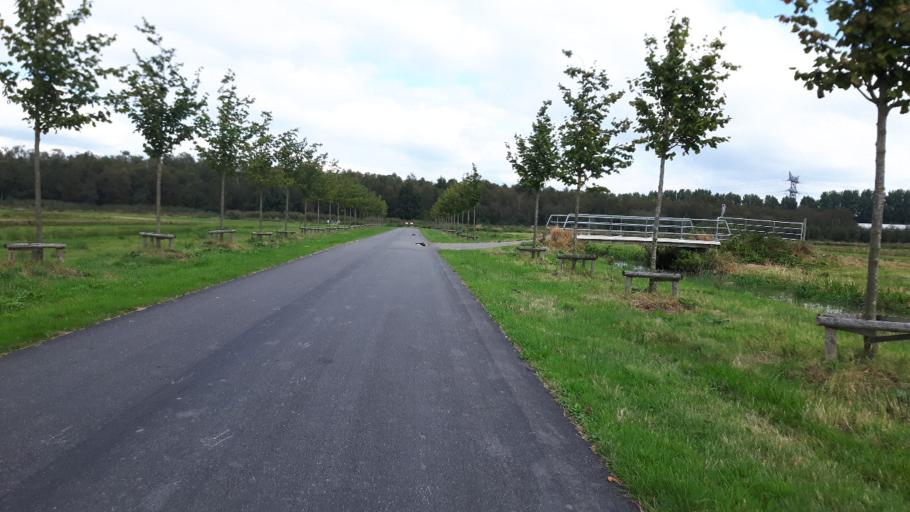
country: NL
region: Utrecht
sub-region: Stichtse Vecht
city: Spechtenkamp
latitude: 52.1277
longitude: 5.0088
